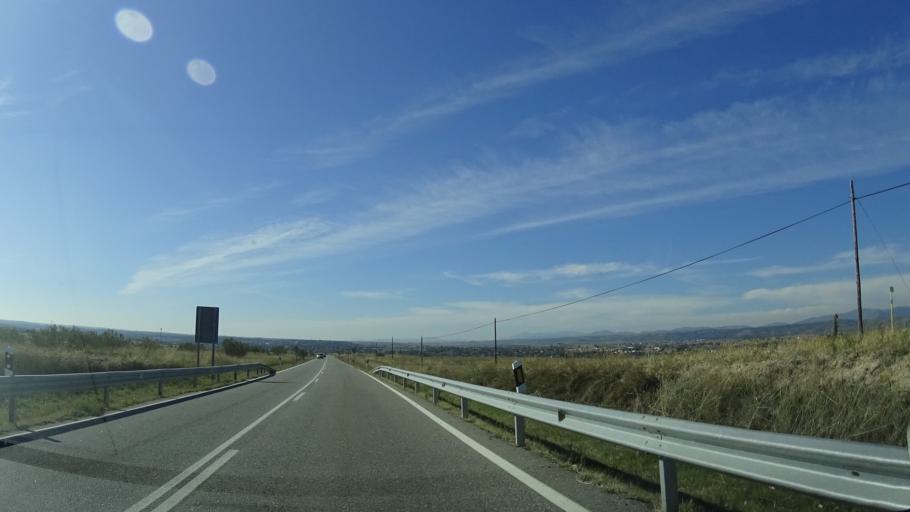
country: ES
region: Madrid
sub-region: Provincia de Madrid
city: Las Rozas de Madrid
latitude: 40.4924
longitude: -3.9154
